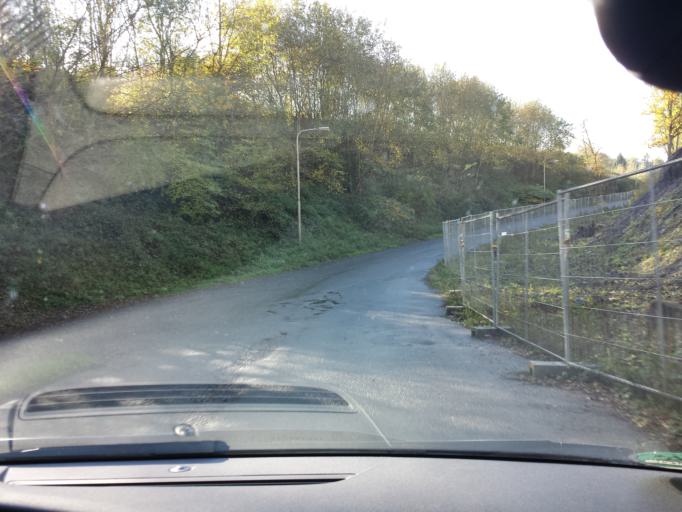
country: NL
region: Limburg
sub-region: Gemeente Kerkrade
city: Kerkrade
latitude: 50.8913
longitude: 6.0732
